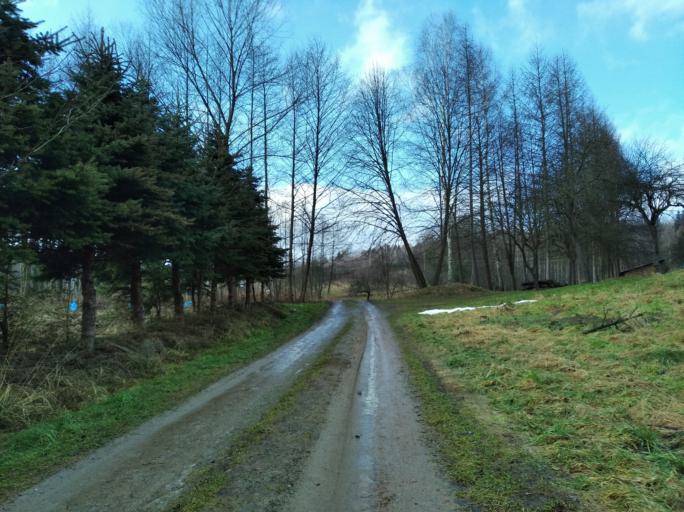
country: PL
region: Subcarpathian Voivodeship
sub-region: Powiat strzyzowski
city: Jawornik
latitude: 49.8331
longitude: 21.8763
